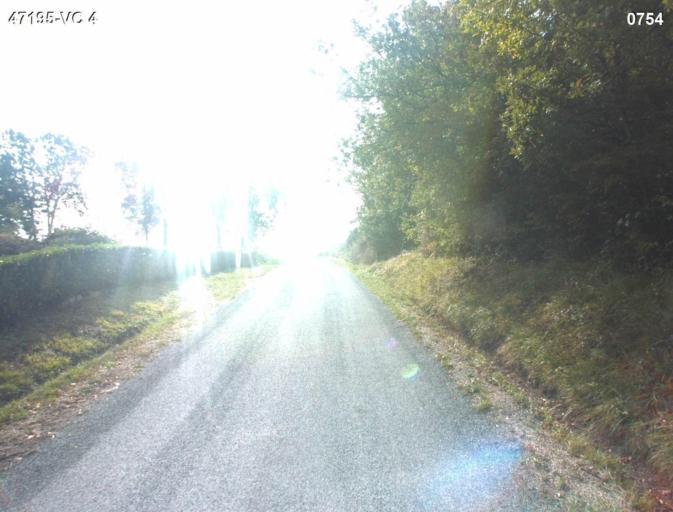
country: FR
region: Aquitaine
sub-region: Departement du Lot-et-Garonne
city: Nerac
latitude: 44.1146
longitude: 0.3799
